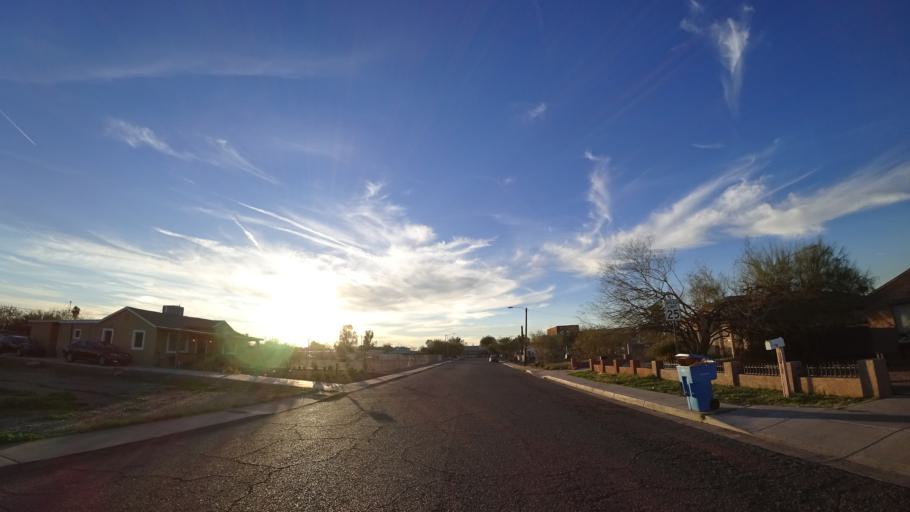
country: US
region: Arizona
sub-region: Maricopa County
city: Phoenix
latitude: 33.4350
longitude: -112.0568
